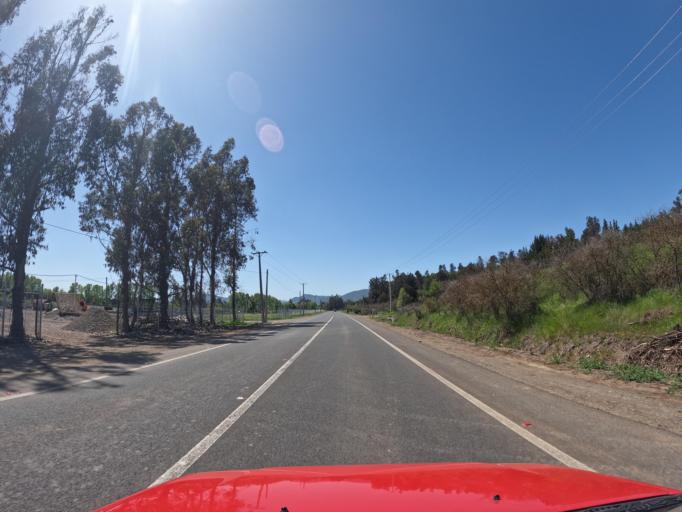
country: CL
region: Maule
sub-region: Provincia de Linares
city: Colbun
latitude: -35.7196
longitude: -71.4108
